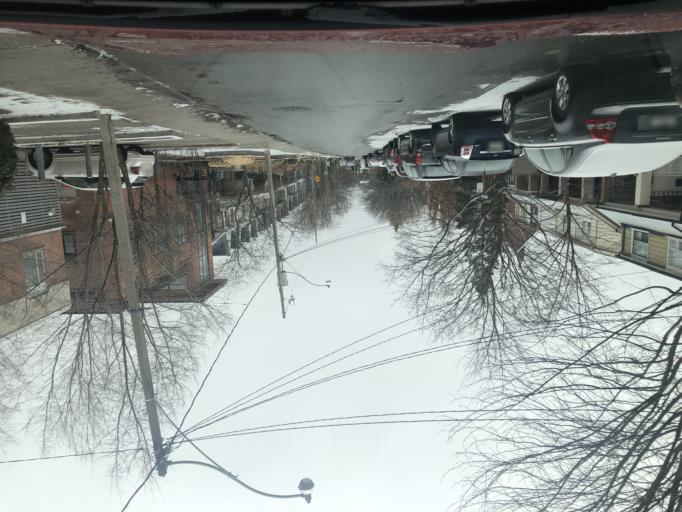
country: CA
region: Ontario
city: Toronto
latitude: 43.6787
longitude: -79.3414
